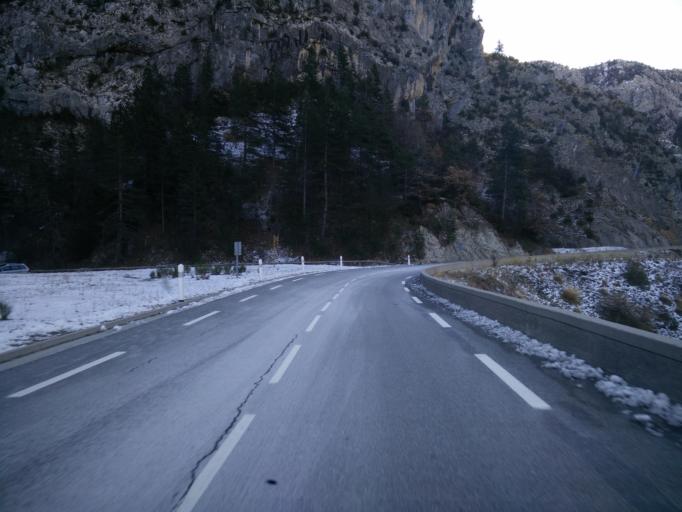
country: FR
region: Provence-Alpes-Cote d'Azur
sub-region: Departement des Alpes-de-Haute-Provence
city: Annot
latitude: 43.9423
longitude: 6.6899
